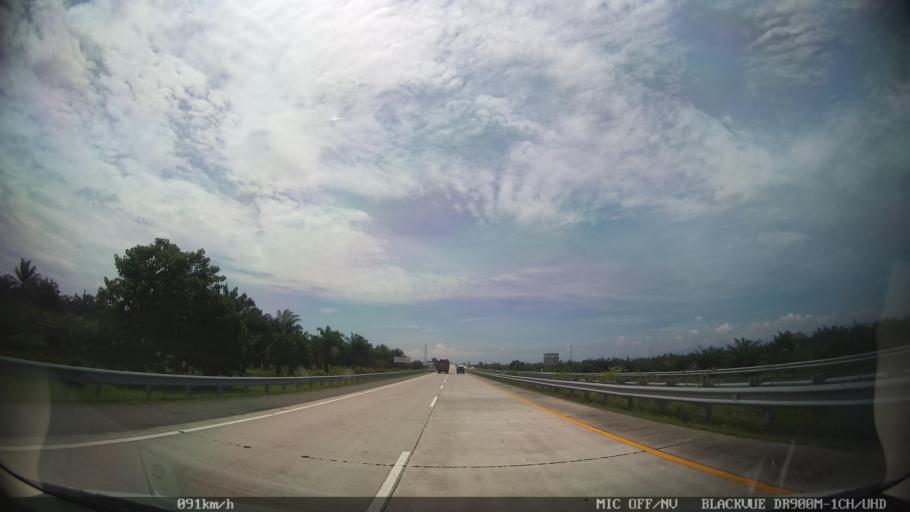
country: ID
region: North Sumatra
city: Percut
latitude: 3.5859
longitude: 98.8452
